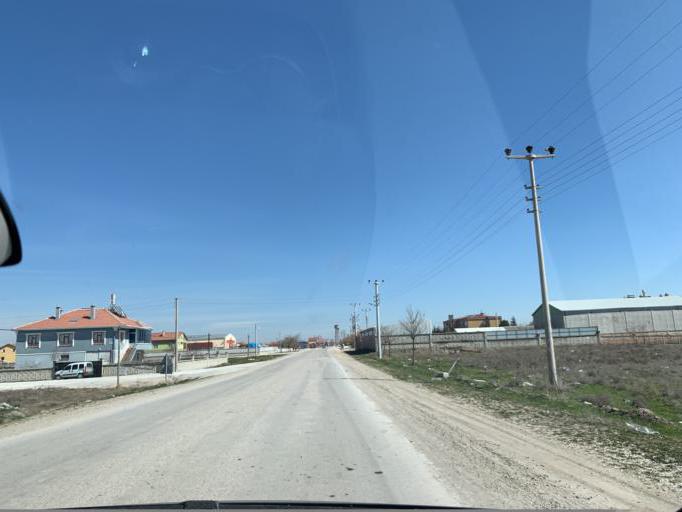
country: TR
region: Konya
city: Yarma
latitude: 37.7504
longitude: 32.8514
